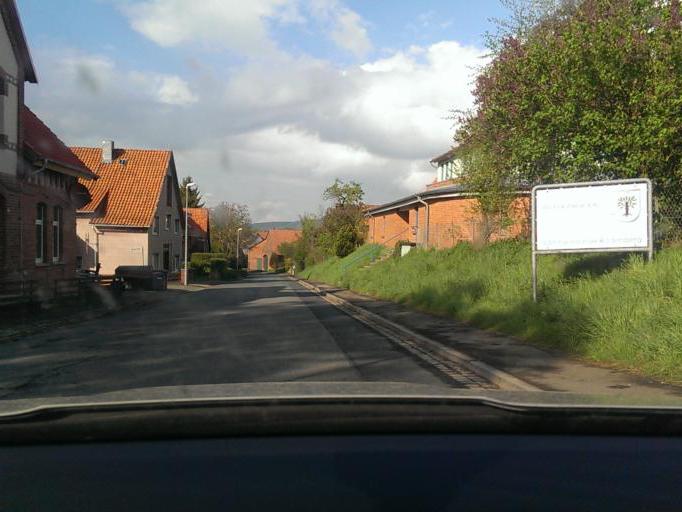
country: DE
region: Lower Saxony
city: Pohle
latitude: 52.2594
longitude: 9.3337
